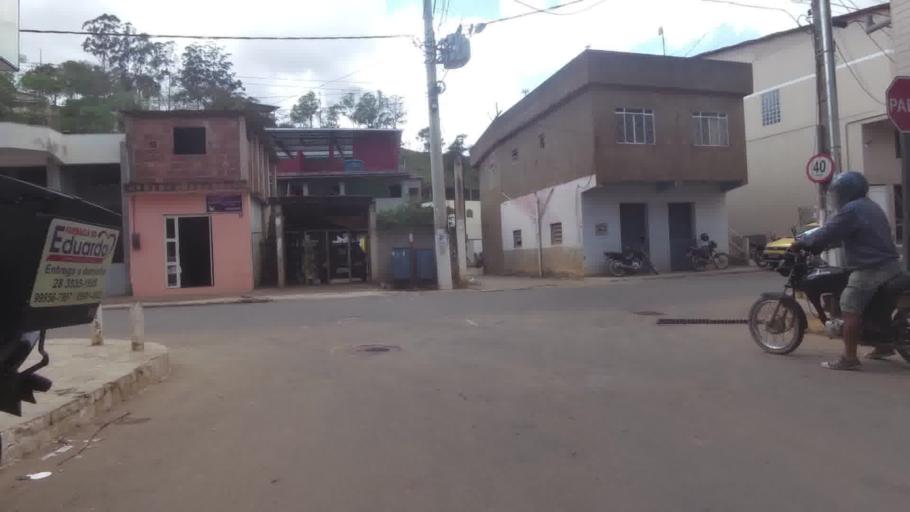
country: BR
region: Espirito Santo
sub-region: Marataizes
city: Marataizes
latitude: -21.1005
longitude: -41.0442
